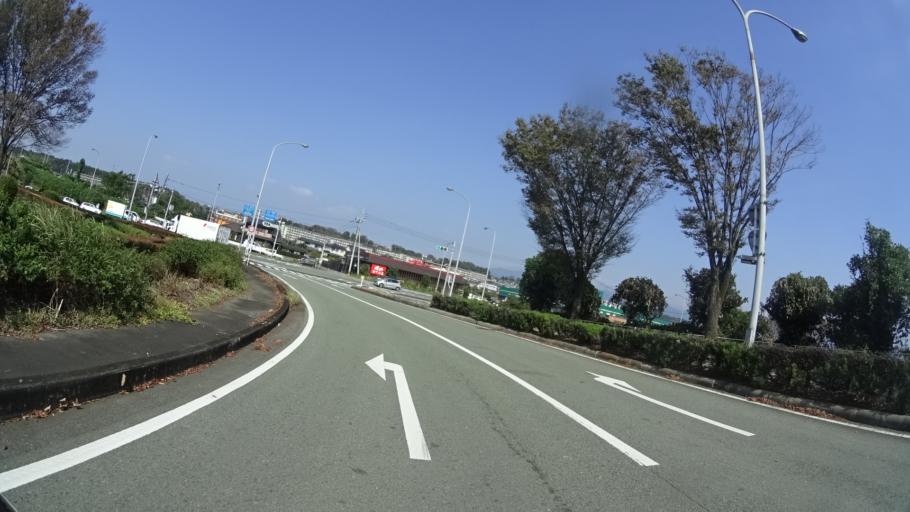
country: JP
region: Kumamoto
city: Ozu
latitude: 32.8749
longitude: 130.8552
